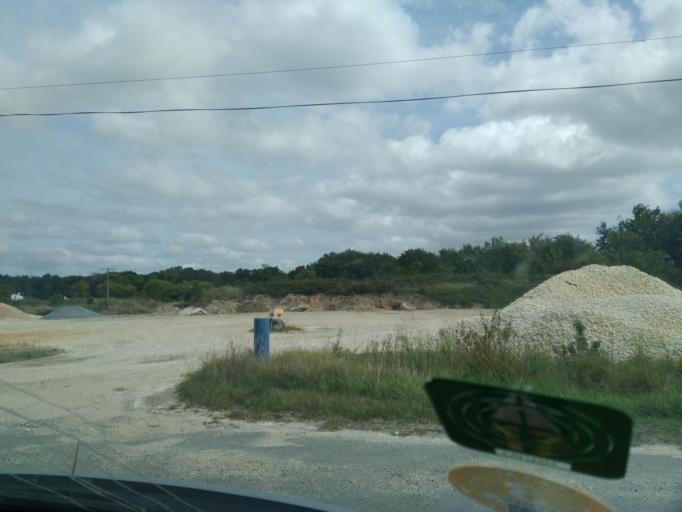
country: FR
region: Poitou-Charentes
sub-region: Departement de la Charente-Maritime
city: Chaillevette
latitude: 45.7132
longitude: -1.0703
